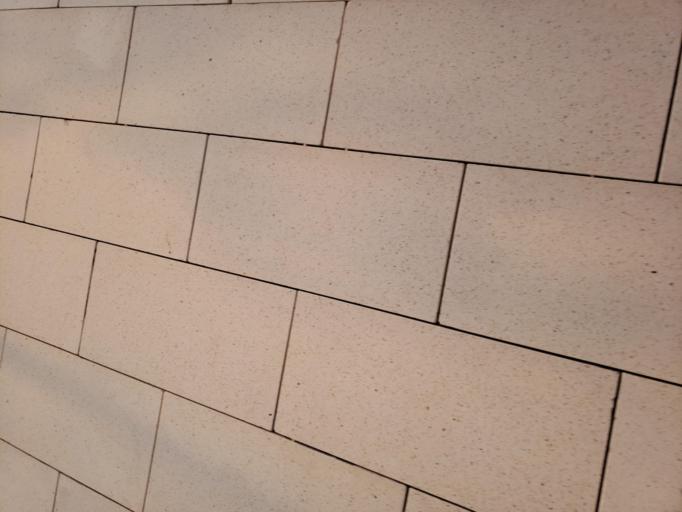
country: AE
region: Dubai
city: Dubai
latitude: 24.9814
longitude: 55.0260
